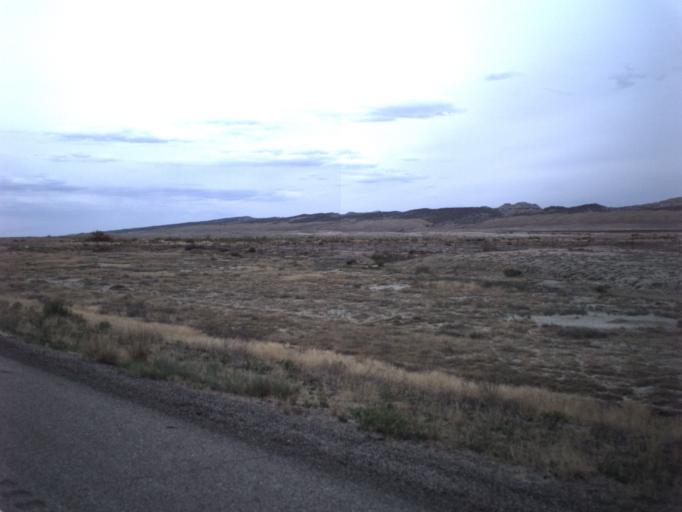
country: US
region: Utah
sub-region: Carbon County
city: East Carbon City
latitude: 39.2310
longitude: -110.3388
